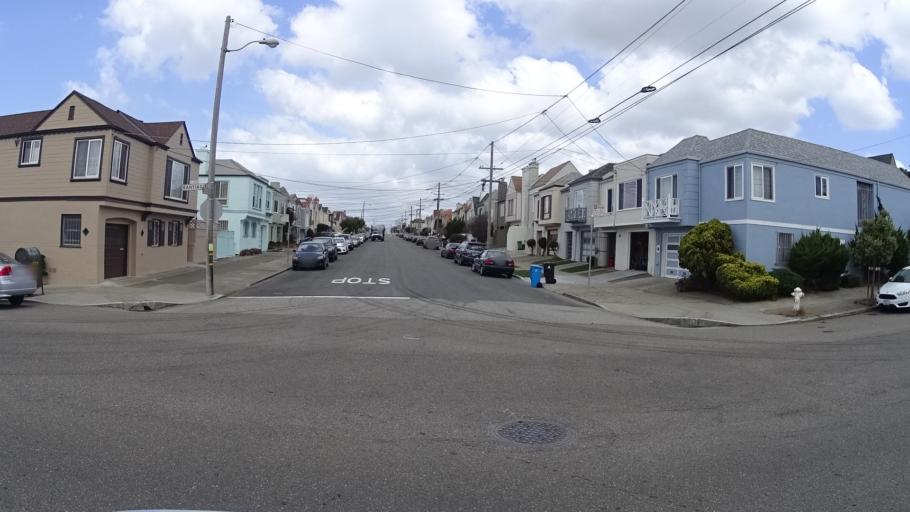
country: US
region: California
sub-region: San Mateo County
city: Daly City
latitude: 37.7442
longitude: -122.4930
